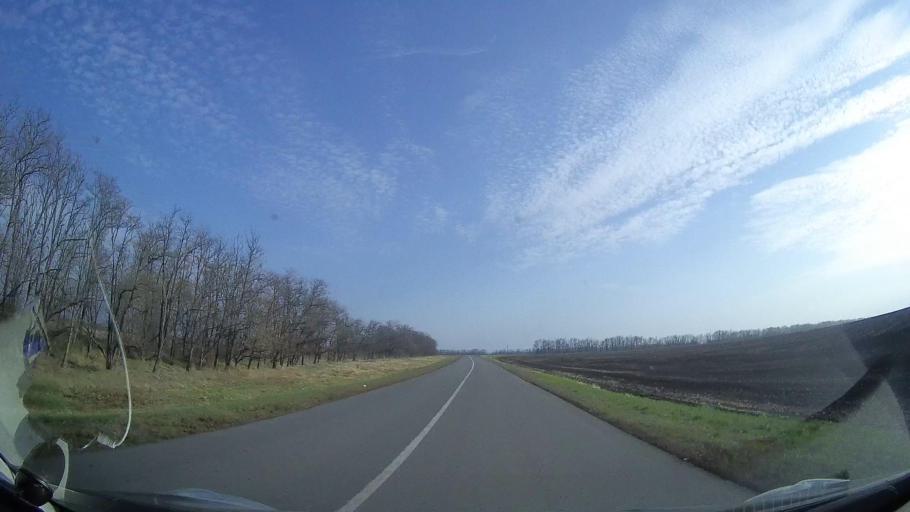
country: RU
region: Rostov
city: Mechetinskaya
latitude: 46.9053
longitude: 40.5372
